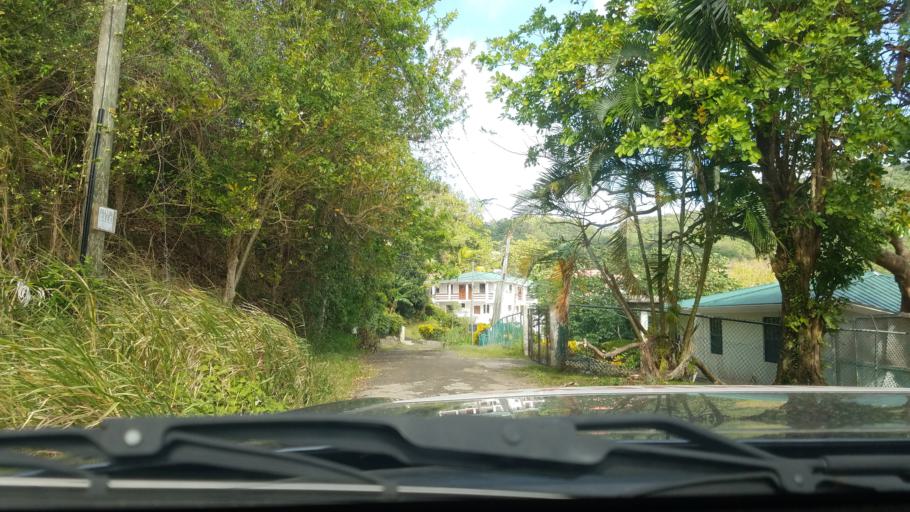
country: LC
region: Gros-Islet
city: Gros Islet
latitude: 14.0390
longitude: -60.9458
